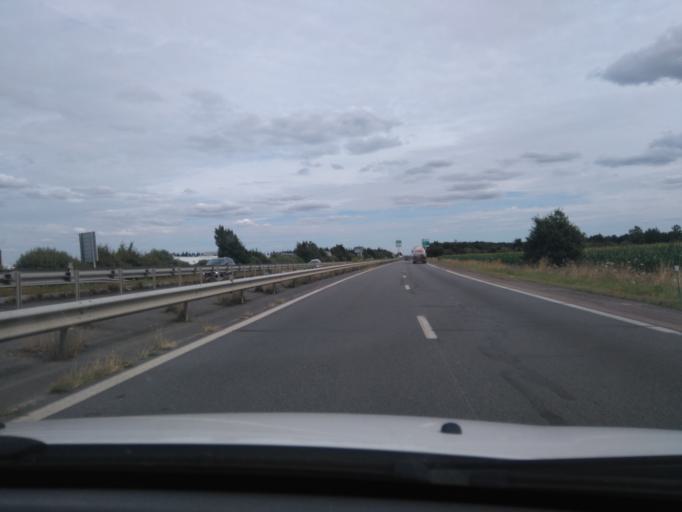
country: FR
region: Brittany
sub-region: Departement des Cotes-d'Armor
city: Plestan
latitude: 48.4160
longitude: -2.4345
